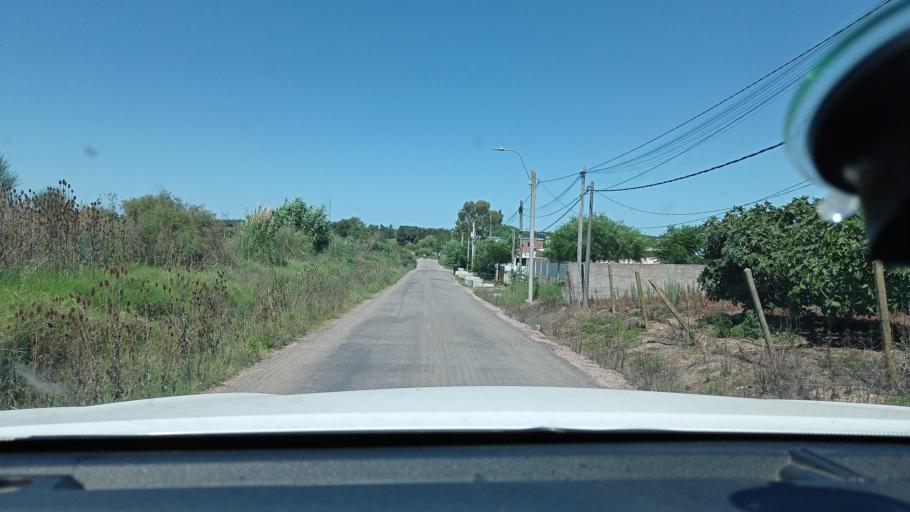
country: UY
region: Canelones
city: Las Piedras
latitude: -34.7411
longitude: -56.2146
